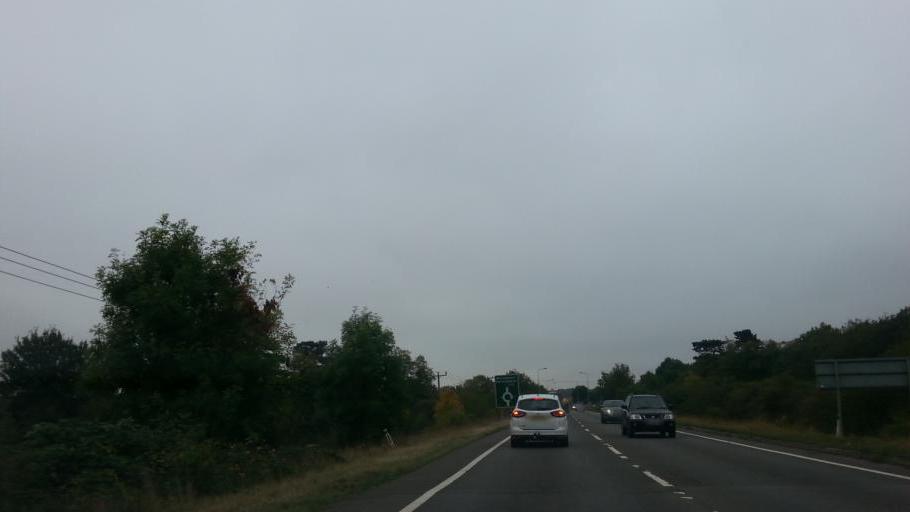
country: GB
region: England
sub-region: Northamptonshire
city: Stanwick
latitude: 52.3340
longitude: -0.5741
